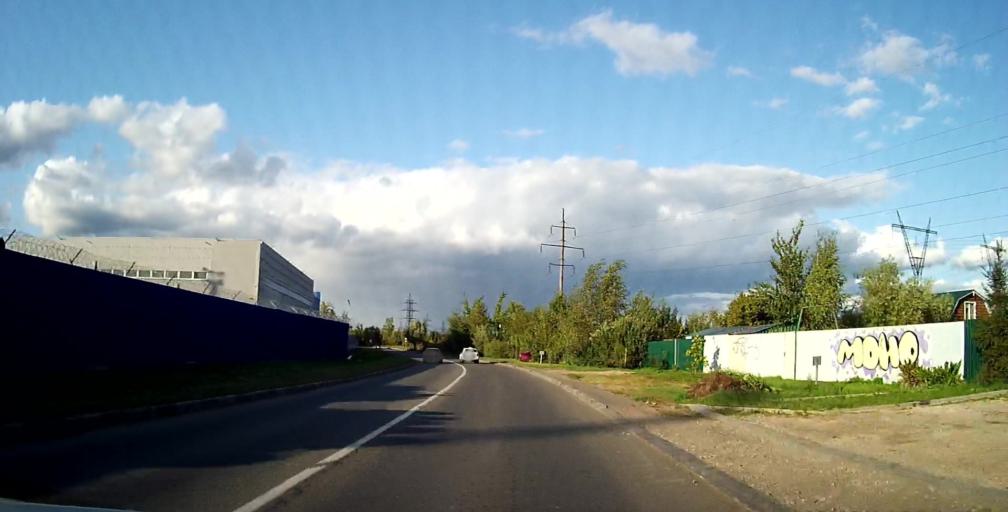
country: RU
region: Moskovskaya
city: Klimovsk
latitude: 55.3683
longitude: 37.5672
